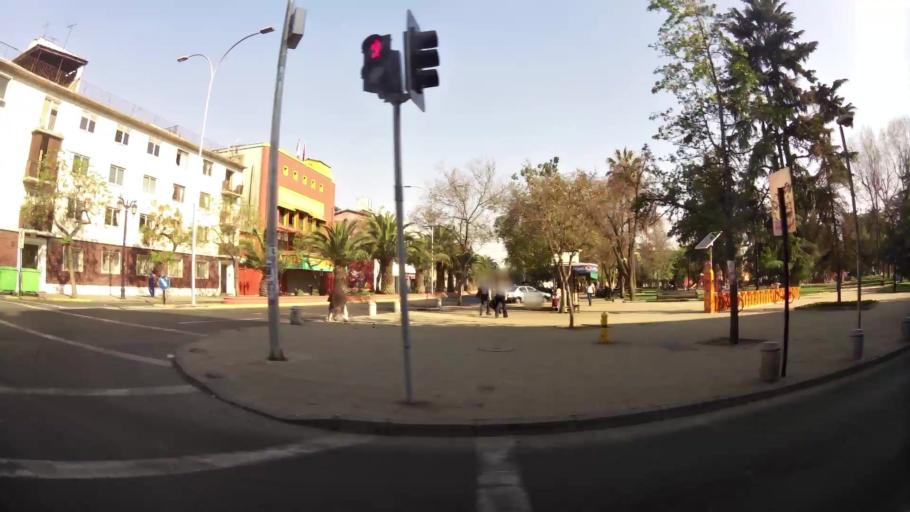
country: CL
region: Santiago Metropolitan
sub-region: Provincia de Santiago
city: Santiago
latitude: -33.4399
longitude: -70.6651
